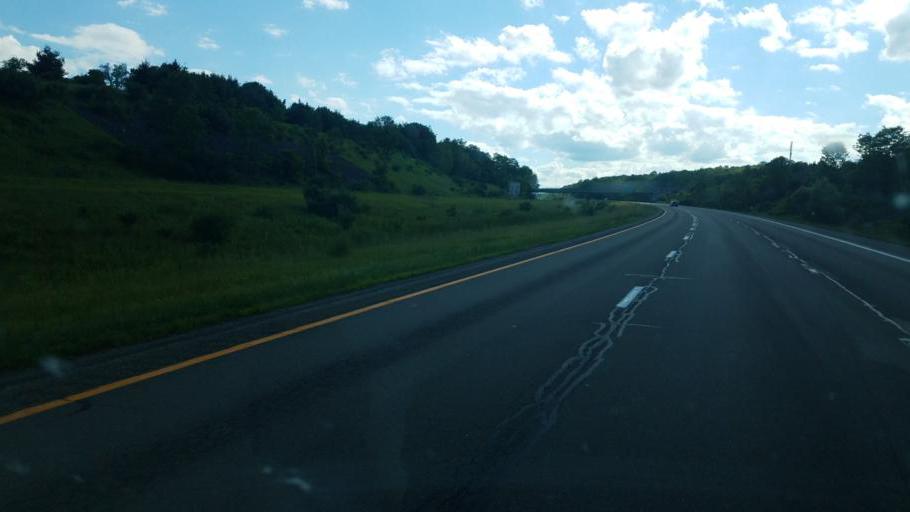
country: US
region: New York
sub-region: Steuben County
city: Hornell
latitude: 42.3659
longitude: -77.6954
